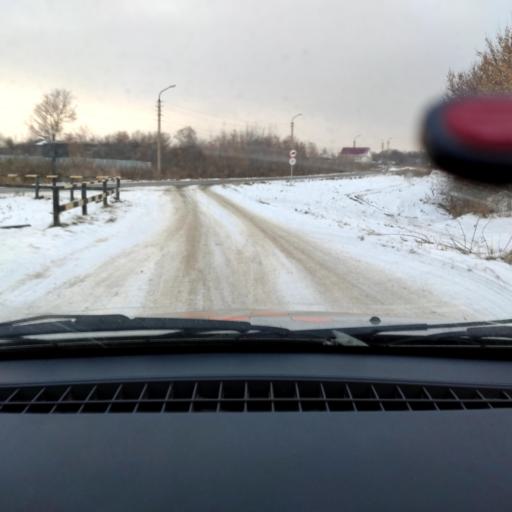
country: RU
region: Bashkortostan
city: Blagoveshchensk
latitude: 54.8888
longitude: 56.0387
